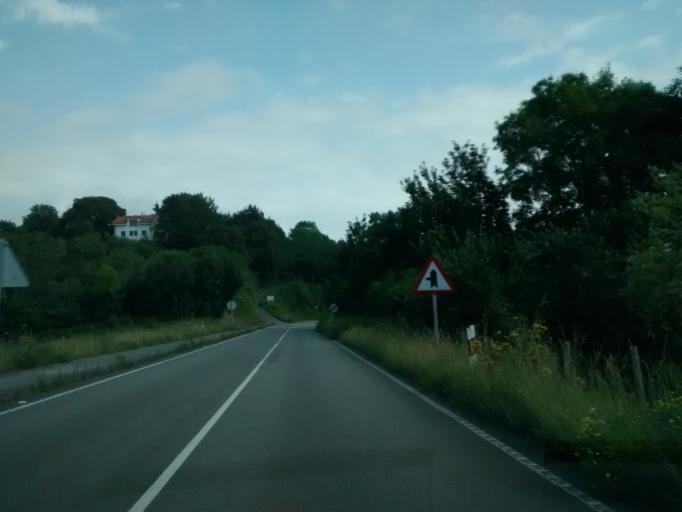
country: ES
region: Asturias
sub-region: Province of Asturias
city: Santa Eulalia
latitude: 43.3951
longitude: -5.4185
